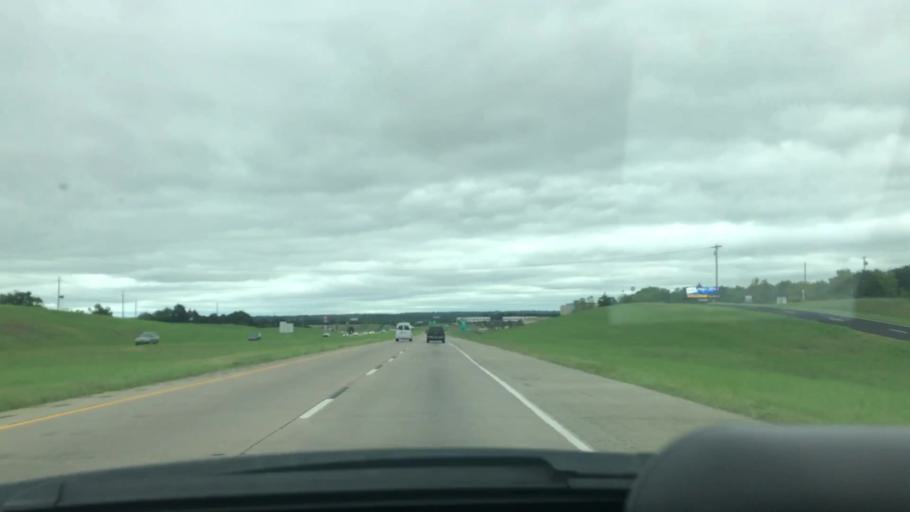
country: US
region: Texas
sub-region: Grayson County
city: Sherman
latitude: 33.6995
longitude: -96.5953
